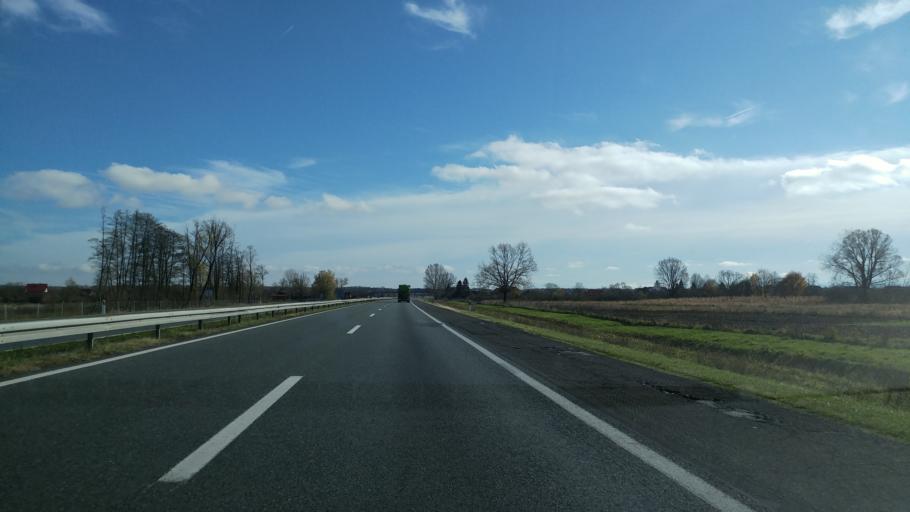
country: HR
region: Sisacko-Moslavacka
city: Lipovljani
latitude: 45.3625
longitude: 16.8982
